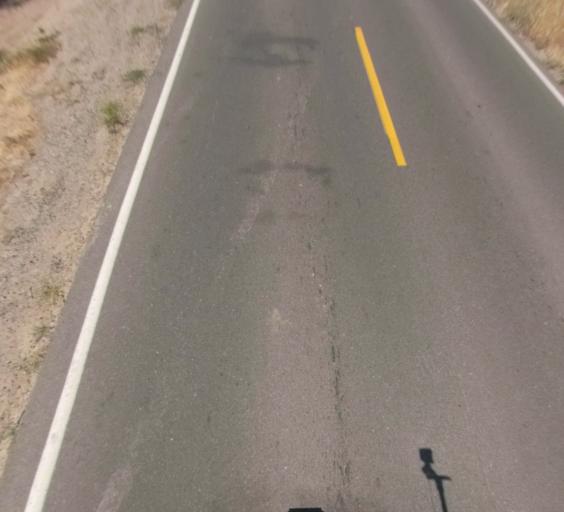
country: US
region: California
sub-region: Madera County
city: Madera Acres
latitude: 37.0356
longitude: -120.0290
